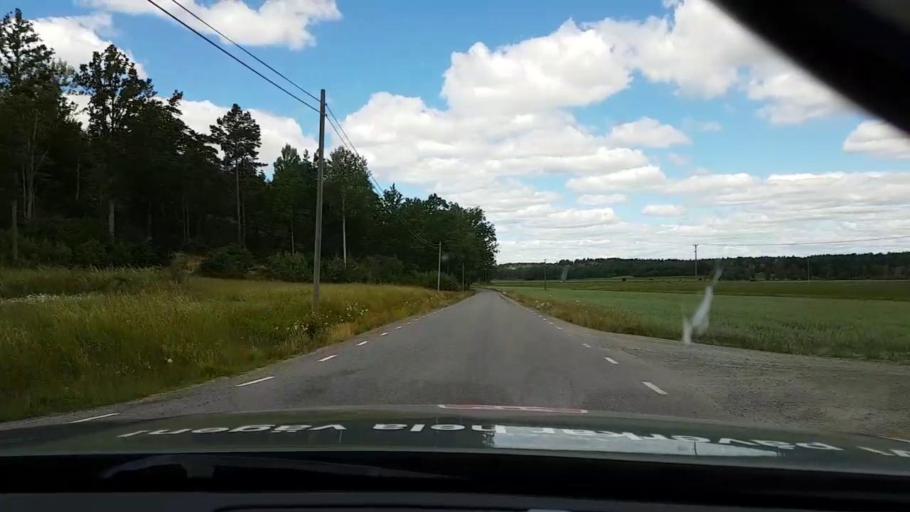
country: SE
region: Kalmar
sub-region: Vasterviks Kommun
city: Forserum
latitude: 57.9869
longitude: 16.6062
